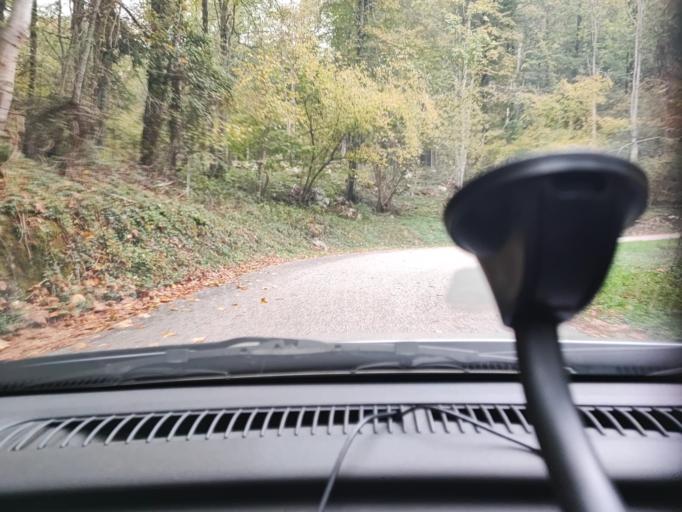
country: SI
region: Kanal
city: Kanal
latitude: 46.0751
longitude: 13.6492
